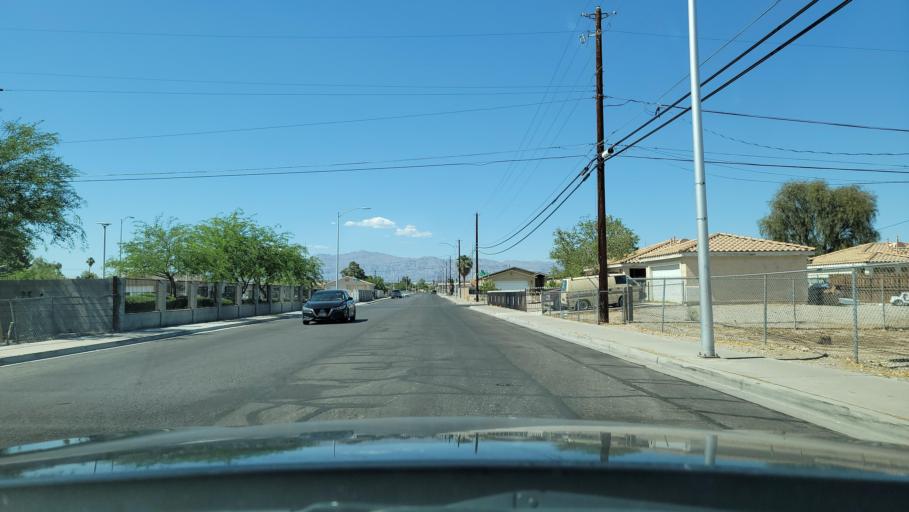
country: US
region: Nevada
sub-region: Clark County
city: Las Vegas
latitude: 36.1987
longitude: -115.1585
